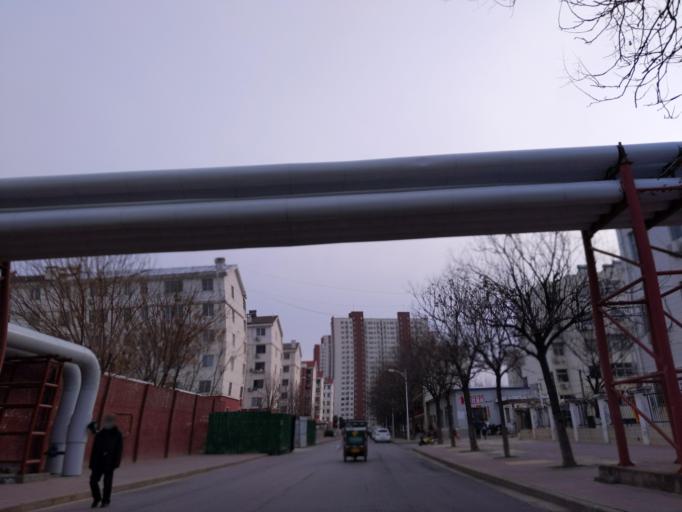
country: CN
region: Henan Sheng
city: Puyang
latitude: 35.7534
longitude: 115.0386
